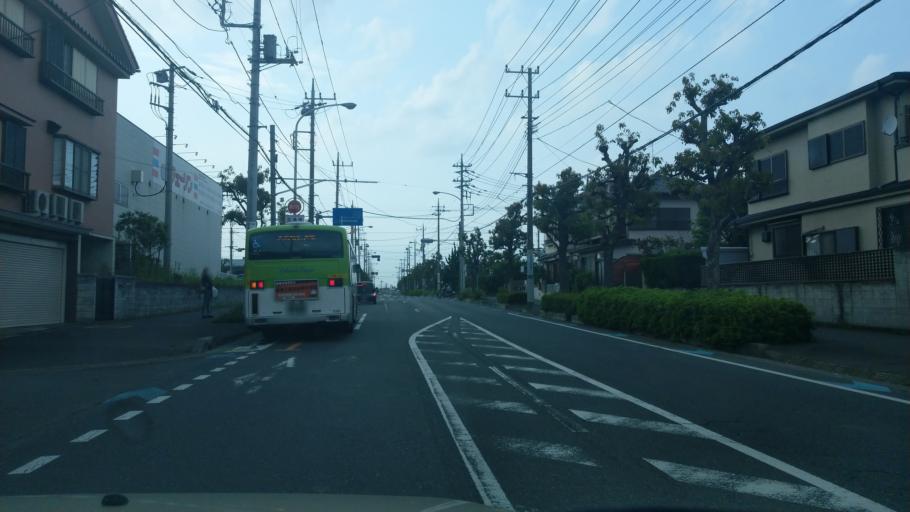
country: JP
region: Saitama
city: Saitama
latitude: 35.8843
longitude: 139.6876
